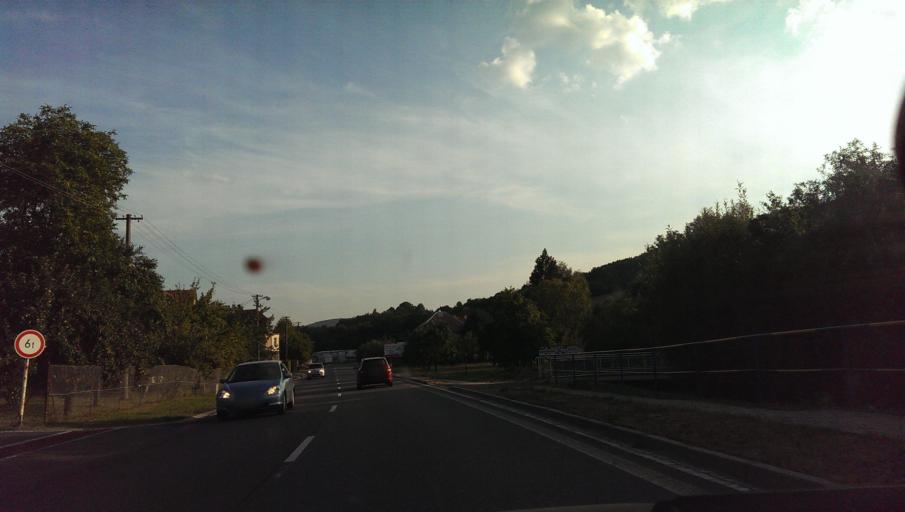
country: CZ
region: Zlin
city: Pozlovice
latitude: 49.1508
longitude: 17.8038
